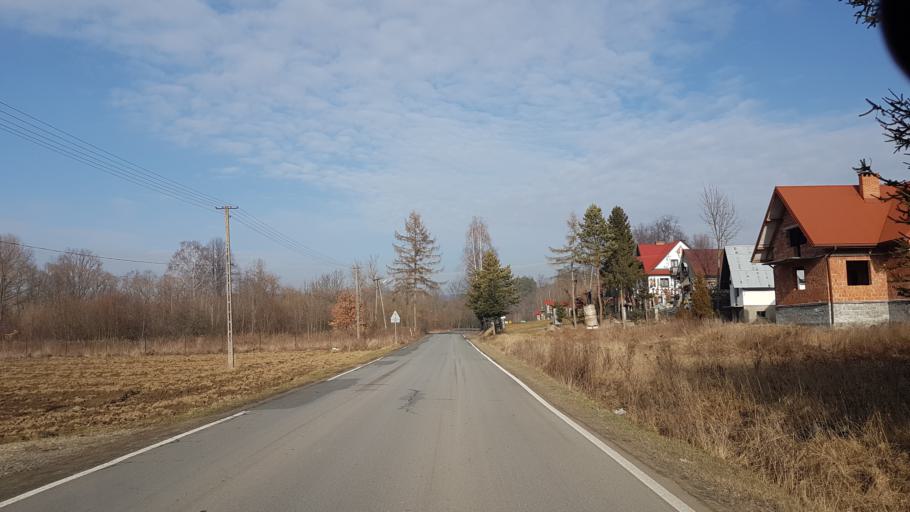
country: PL
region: Lesser Poland Voivodeship
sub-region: Powiat nowosadecki
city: Olszana
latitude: 49.5806
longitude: 20.5388
